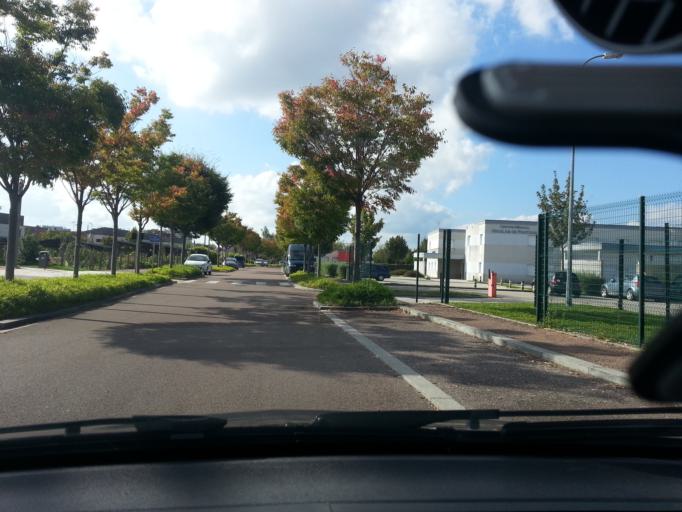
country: FR
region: Bourgogne
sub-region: Departement de Saone-et-Loire
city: Chalon-sur-Saone
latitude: 46.7976
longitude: 4.8546
